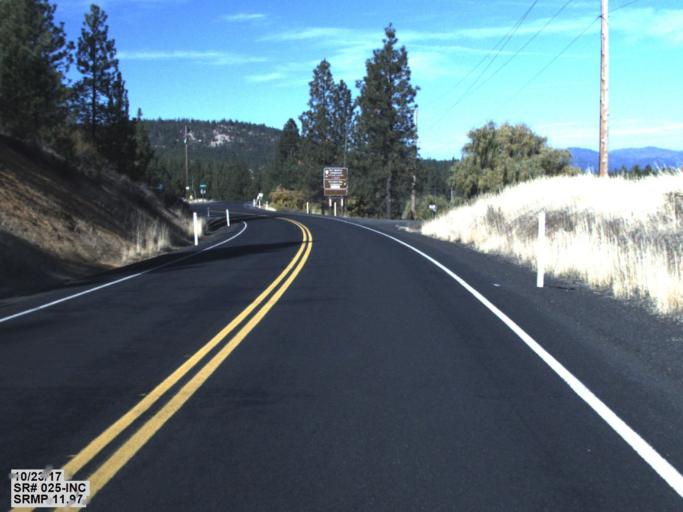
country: US
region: Washington
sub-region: Lincoln County
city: Davenport
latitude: 47.8204
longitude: -118.1829
